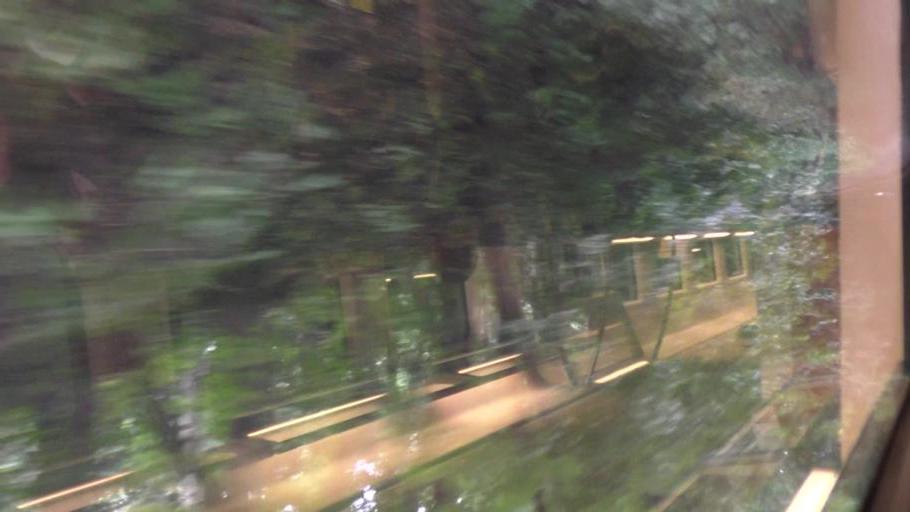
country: DE
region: Saxony
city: Goerlitz
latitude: 51.1426
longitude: 14.9887
